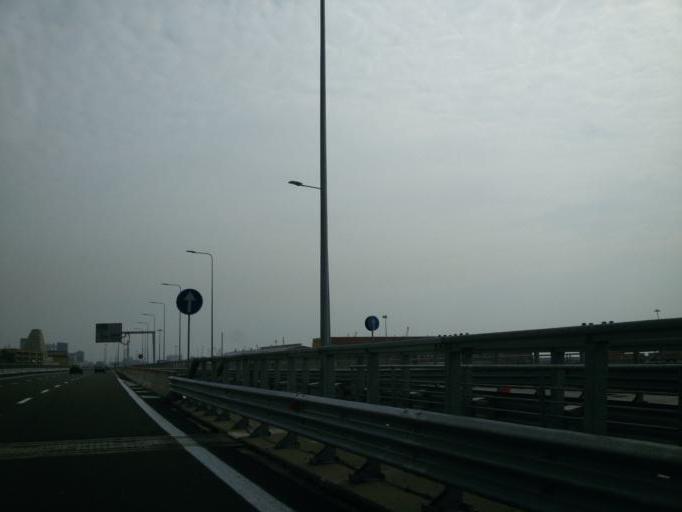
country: IT
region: Liguria
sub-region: Provincia di Genova
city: San Teodoro
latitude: 44.4125
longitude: 8.8760
